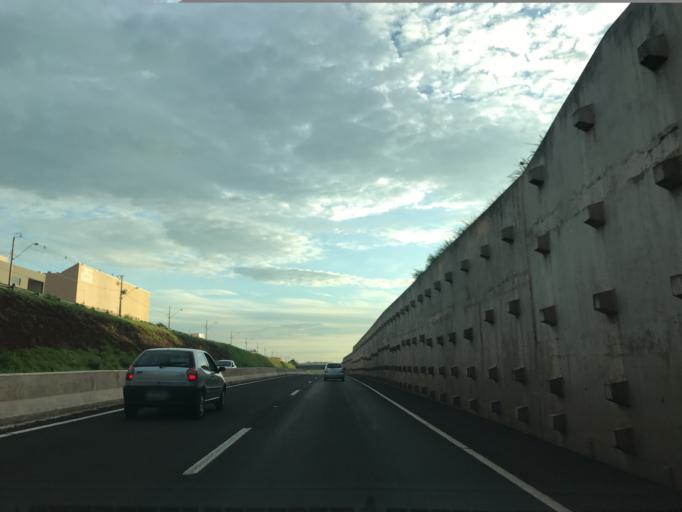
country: BR
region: Parana
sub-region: Maringa
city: Maringa
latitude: -23.3766
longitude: -51.9404
